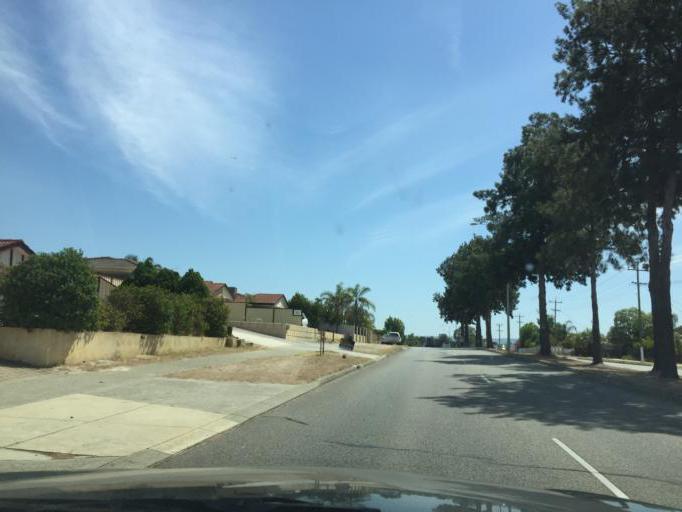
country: AU
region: Western Australia
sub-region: Gosnells
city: Thornlie
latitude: -32.0729
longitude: 115.9640
